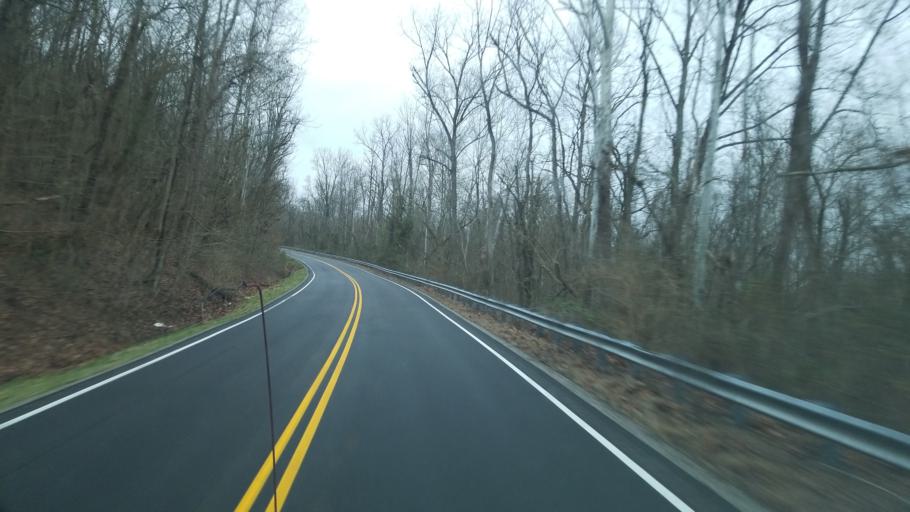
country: US
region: Kentucky
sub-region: Bracken County
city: Augusta
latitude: 38.7797
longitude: -83.9488
